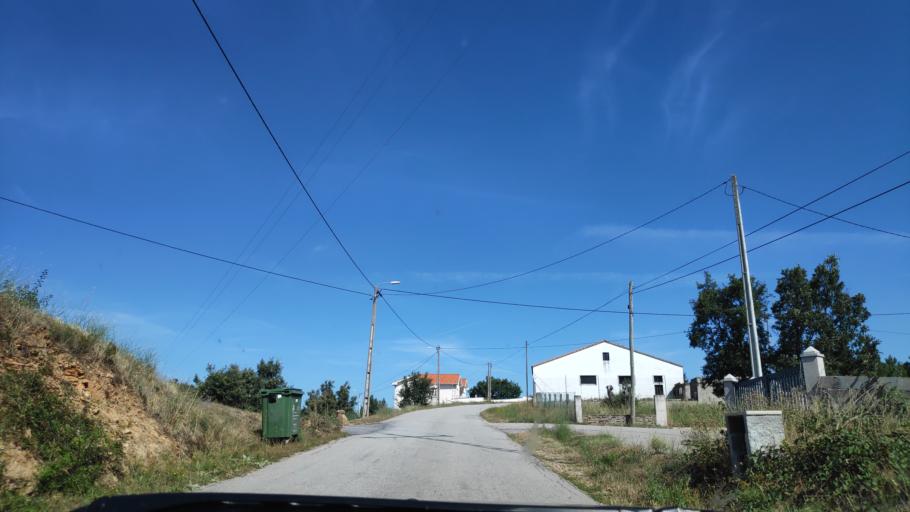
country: ES
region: Castille and Leon
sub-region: Provincia de Zamora
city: Alcanices
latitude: 41.6377
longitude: -6.3544
